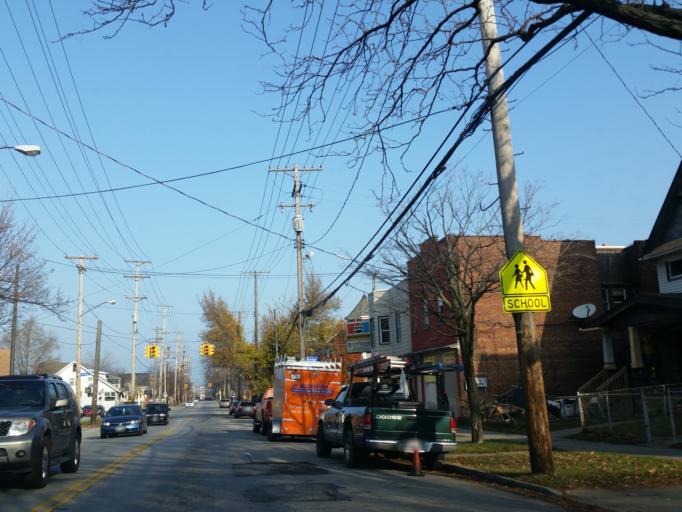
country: US
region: Ohio
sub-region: Cuyahoga County
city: Cleveland
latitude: 41.4803
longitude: -81.7302
